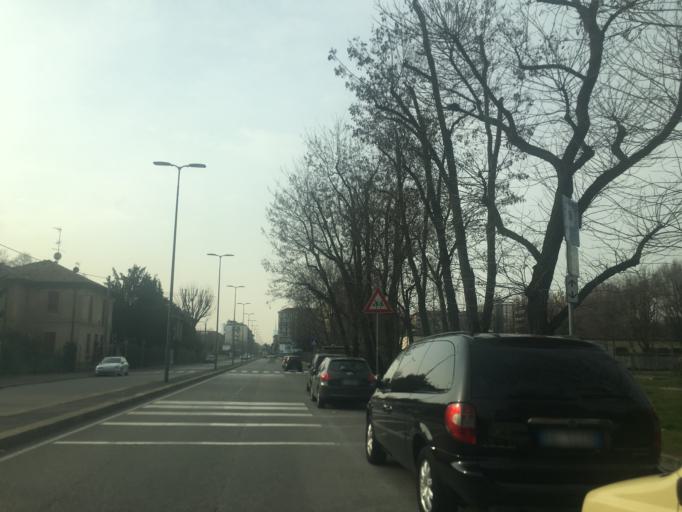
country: IT
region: Lombardy
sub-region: Citta metropolitana di Milano
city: Bresso
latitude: 45.5135
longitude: 9.2074
